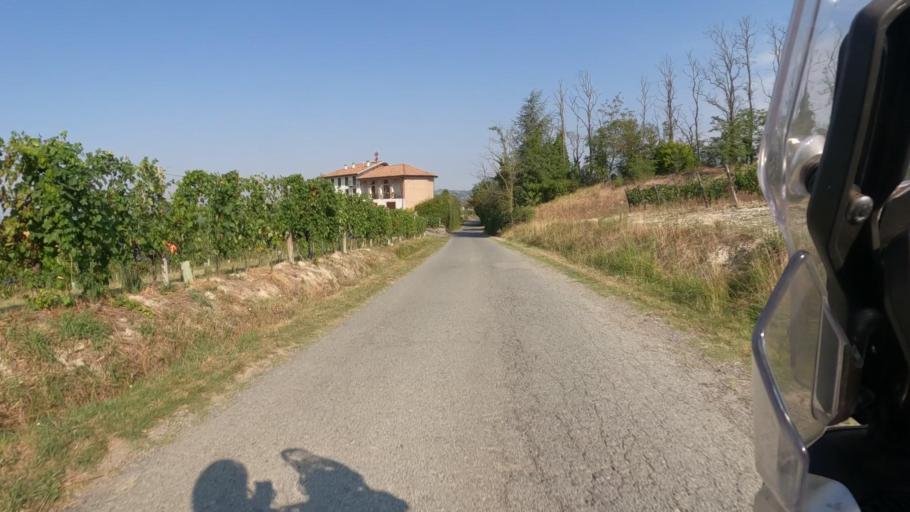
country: IT
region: Piedmont
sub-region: Provincia di Asti
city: Nizza Monferrato
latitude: 44.7580
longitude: 8.3816
